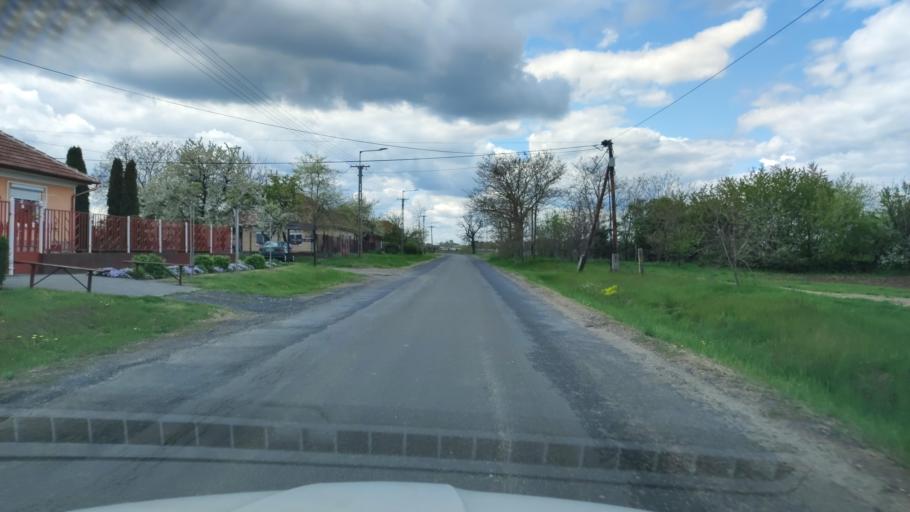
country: HU
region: Pest
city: Cegledbercel
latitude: 47.2128
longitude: 19.7218
